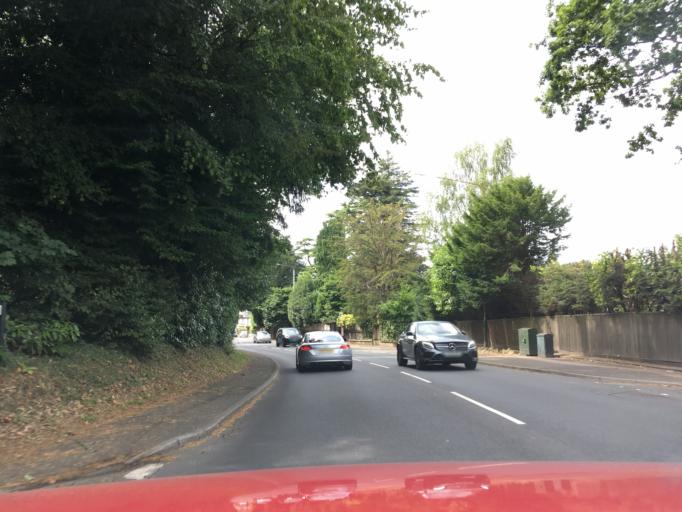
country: GB
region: England
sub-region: Kent
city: Royal Tunbridge Wells
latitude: 51.1308
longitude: 0.2140
